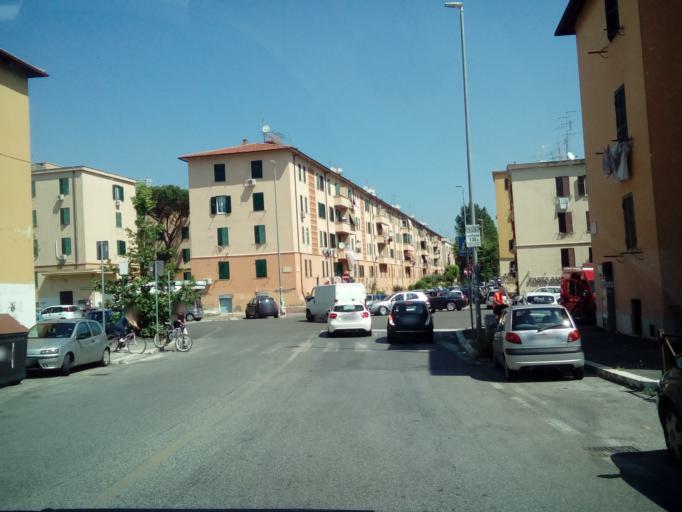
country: IT
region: Latium
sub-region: Citta metropolitana di Roma Capitale
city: Rome
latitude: 41.8894
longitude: 12.5765
